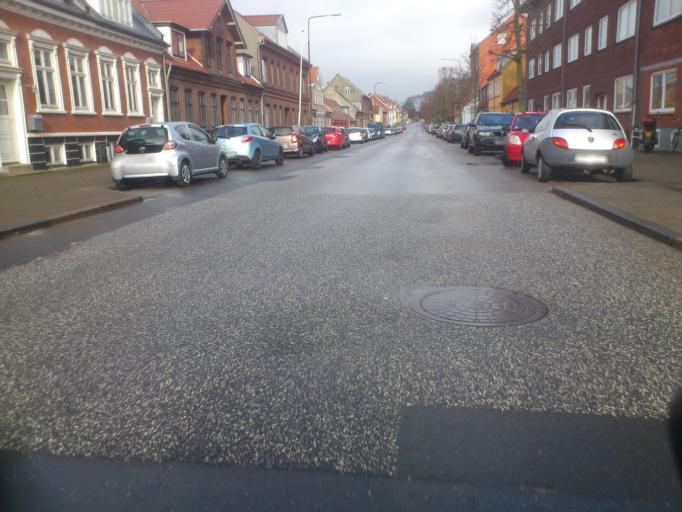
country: DK
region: South Denmark
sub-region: Fredericia Kommune
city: Fredericia
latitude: 55.5640
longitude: 9.7637
